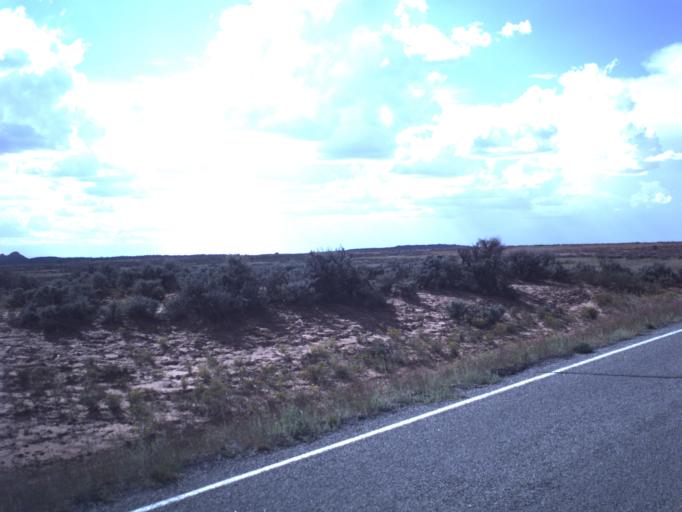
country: US
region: Utah
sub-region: Grand County
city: Moab
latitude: 38.5262
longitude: -109.7462
